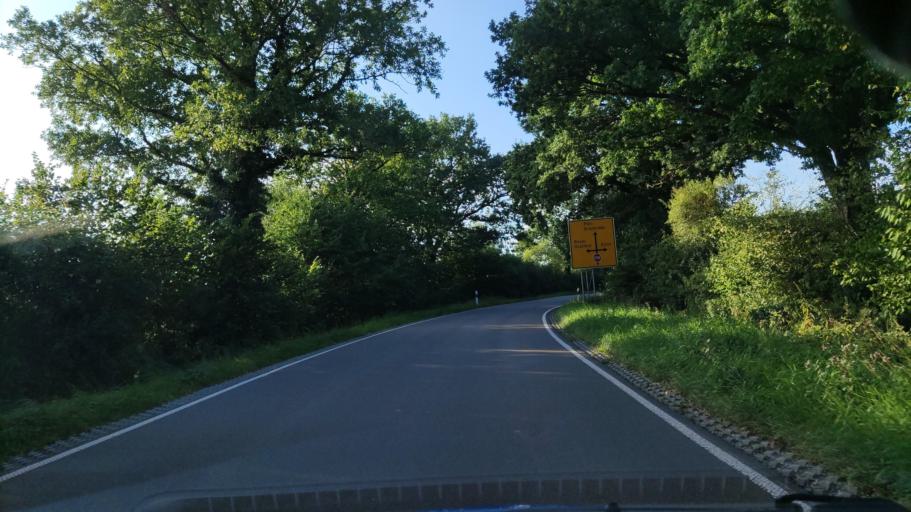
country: DE
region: Schleswig-Holstein
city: Glasau
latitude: 54.0871
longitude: 10.4946
